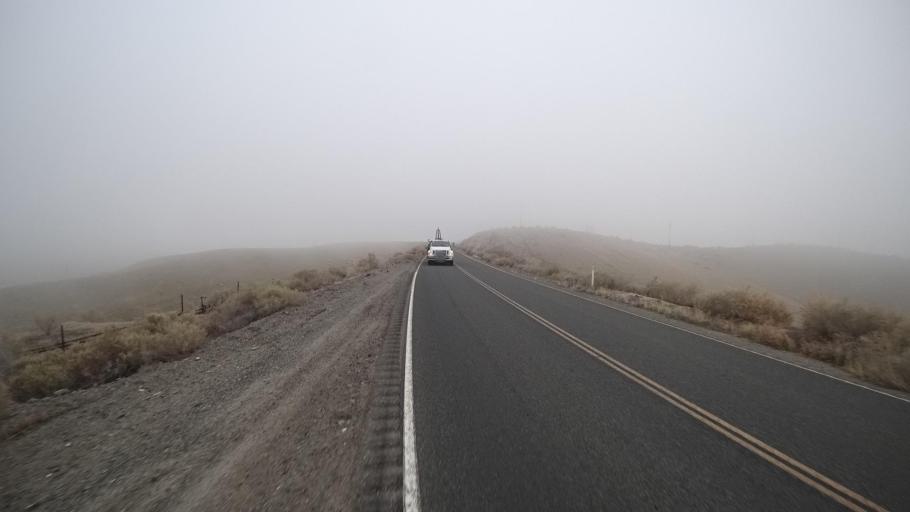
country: US
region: California
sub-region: Kern County
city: Buttonwillow
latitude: 35.3031
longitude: -119.4654
